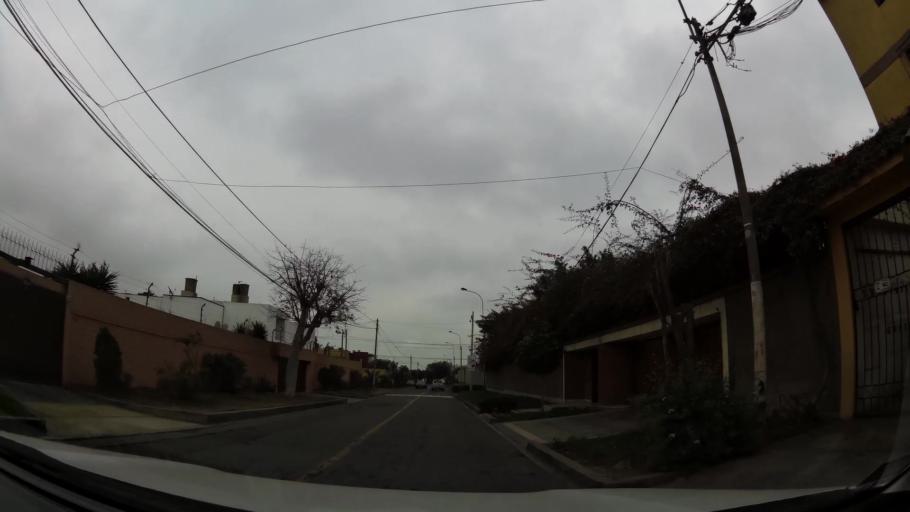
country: PE
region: Lima
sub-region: Lima
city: La Molina
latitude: -12.0687
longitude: -76.9615
